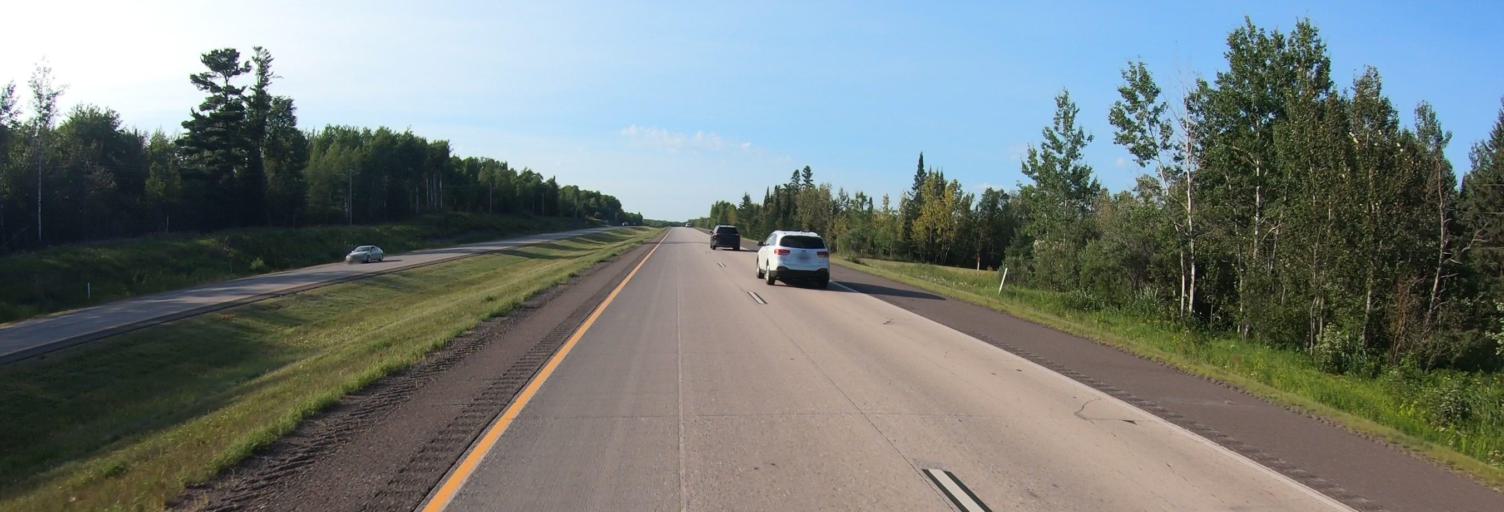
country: US
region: Minnesota
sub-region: Carlton County
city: Cloquet
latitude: 46.9650
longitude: -92.4643
